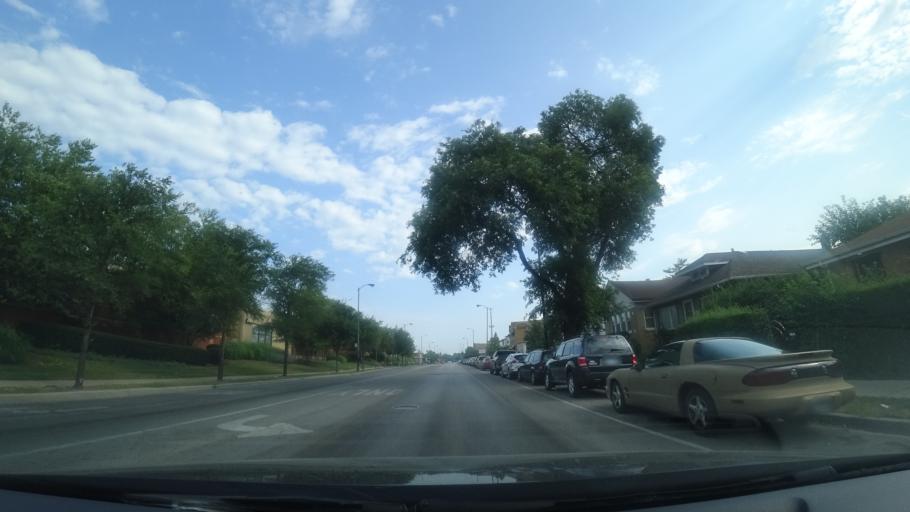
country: US
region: Illinois
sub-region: Cook County
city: Elmwood Park
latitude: 41.9276
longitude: -87.7855
